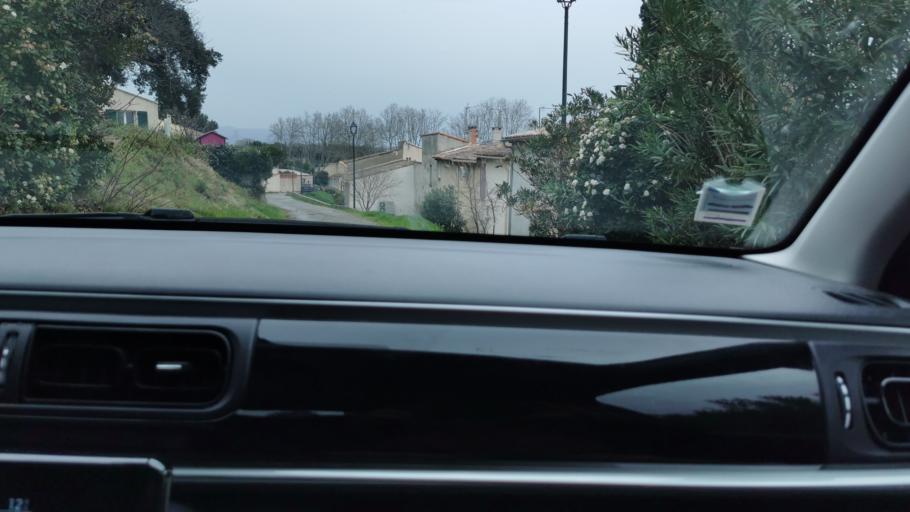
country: FR
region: Provence-Alpes-Cote d'Azur
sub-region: Departement des Bouches-du-Rhone
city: Lamanon
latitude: 43.7018
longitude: 5.0852
